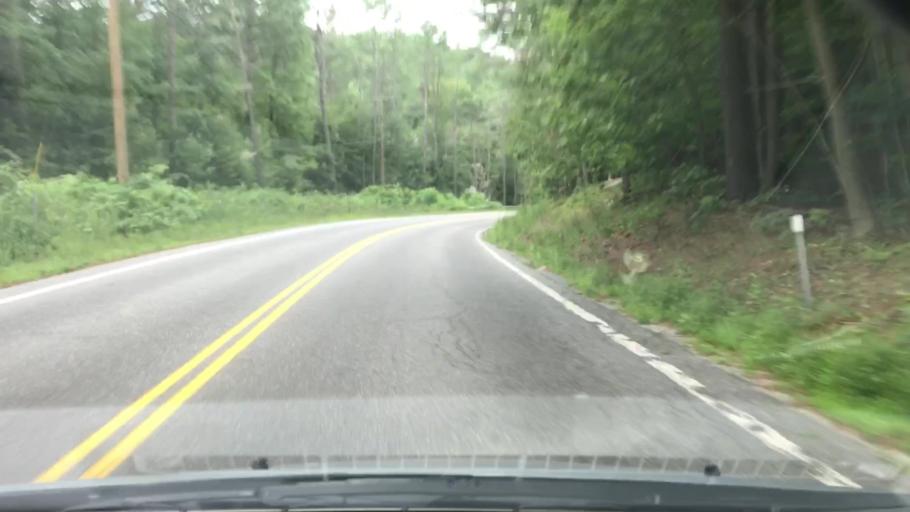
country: US
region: New Hampshire
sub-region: Grafton County
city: North Haverhill
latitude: 44.0692
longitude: -72.0415
